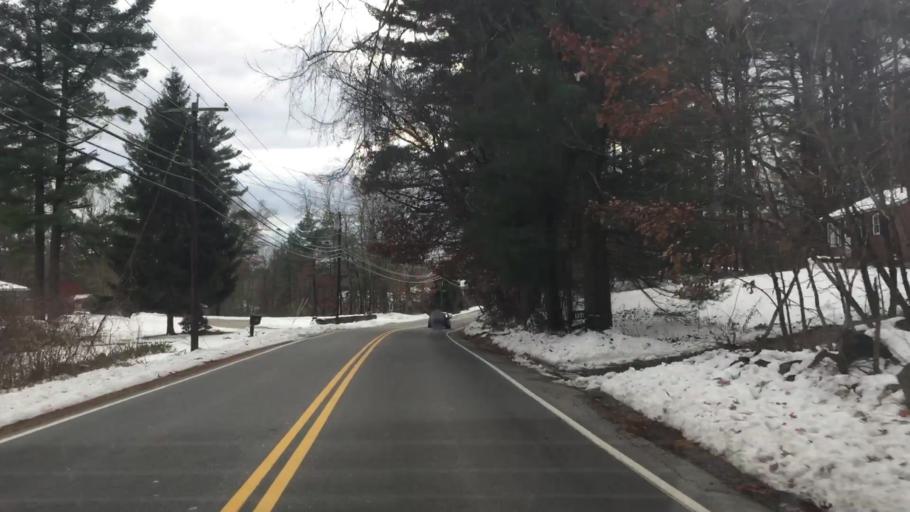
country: US
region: New Hampshire
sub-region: Hillsborough County
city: Pelham
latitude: 42.7140
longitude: -71.3416
